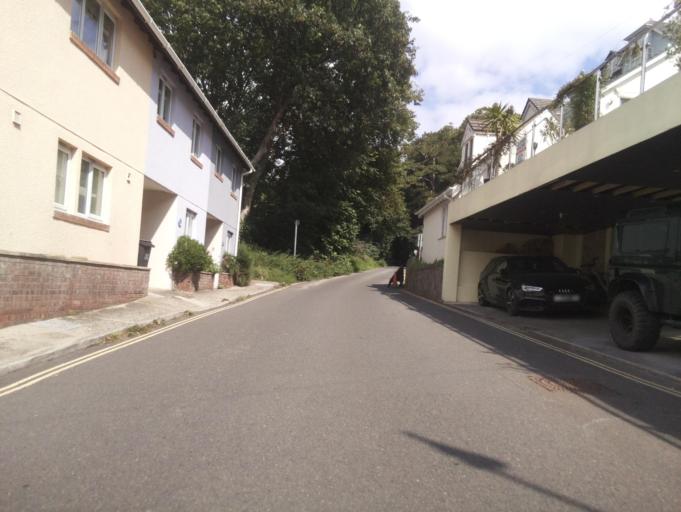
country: GB
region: England
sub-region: Devon
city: Dartmouth
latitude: 50.3520
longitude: -3.5638
